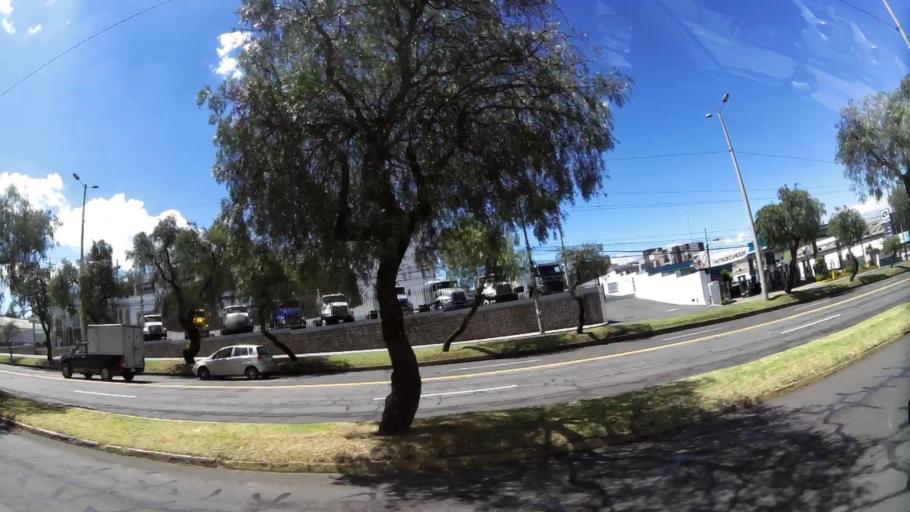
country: EC
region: Pichincha
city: Quito
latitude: -0.1334
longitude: -78.4820
